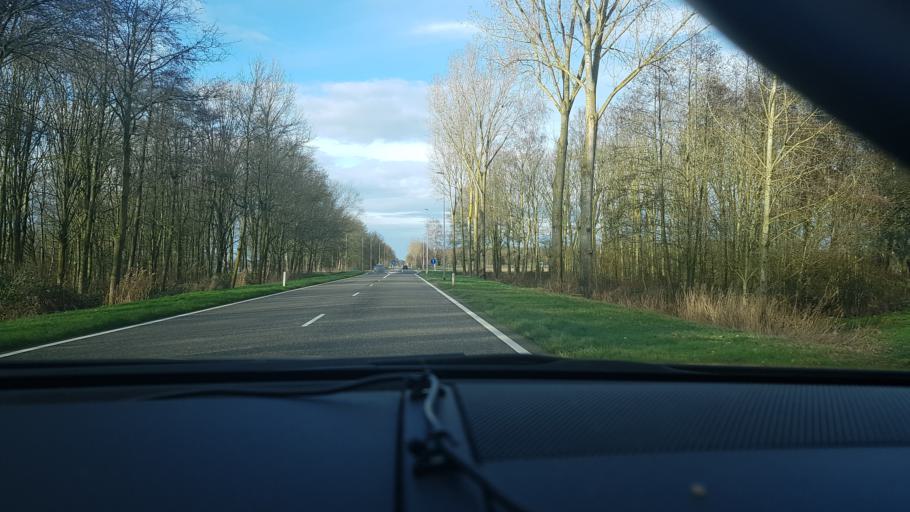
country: NL
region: Limburg
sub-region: Gemeente Peel en Maas
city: Maasbree
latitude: 51.3364
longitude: 6.0338
